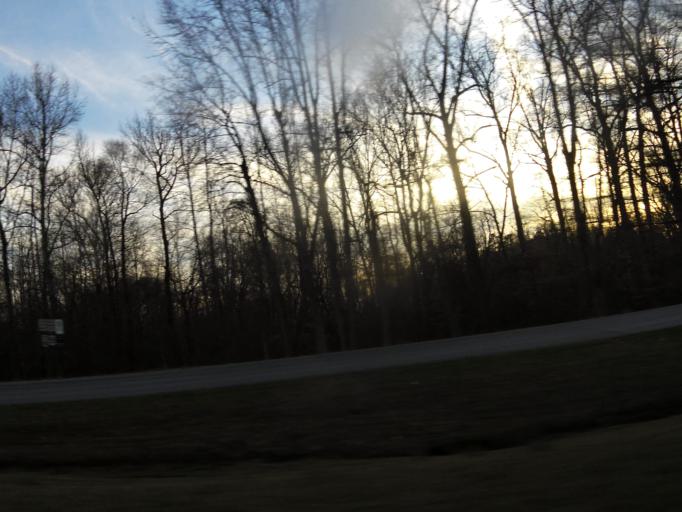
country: US
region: Virginia
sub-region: City of Franklin
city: Franklin
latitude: 36.6836
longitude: -76.9674
